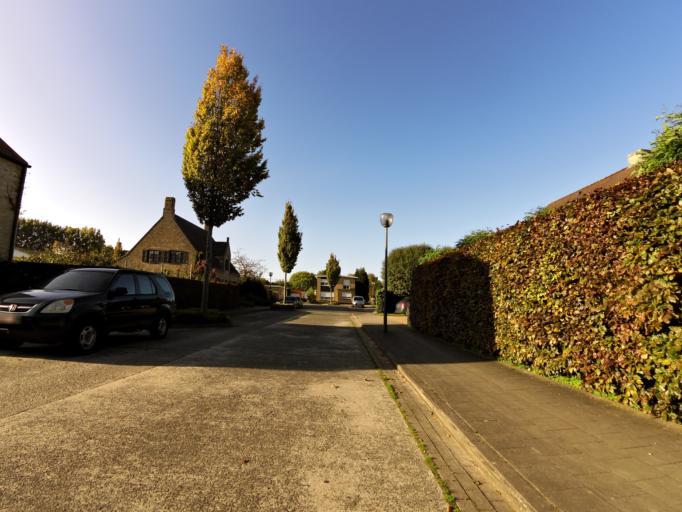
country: BE
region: Flanders
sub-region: Provincie West-Vlaanderen
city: Brugge
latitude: 51.1951
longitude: 3.1904
